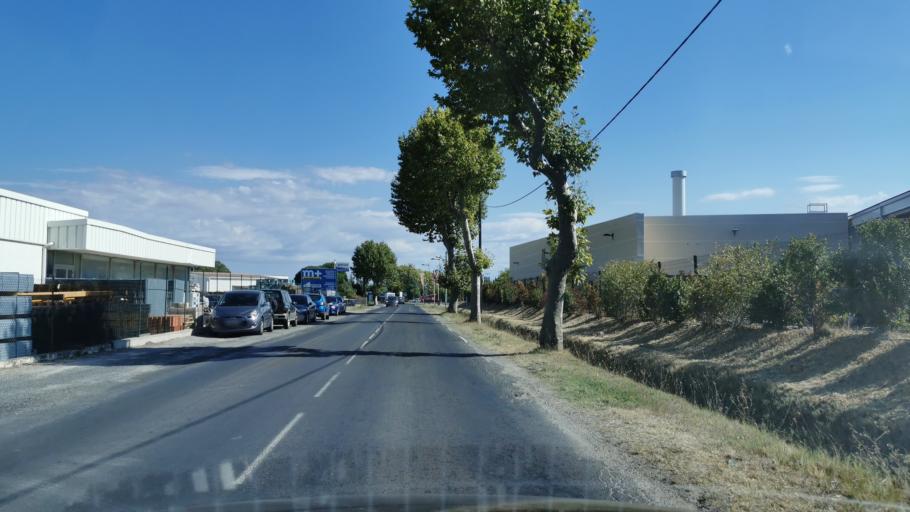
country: FR
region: Languedoc-Roussillon
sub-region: Departement de l'Aude
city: Peyriac-Minervois
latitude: 43.2866
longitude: 2.5712
